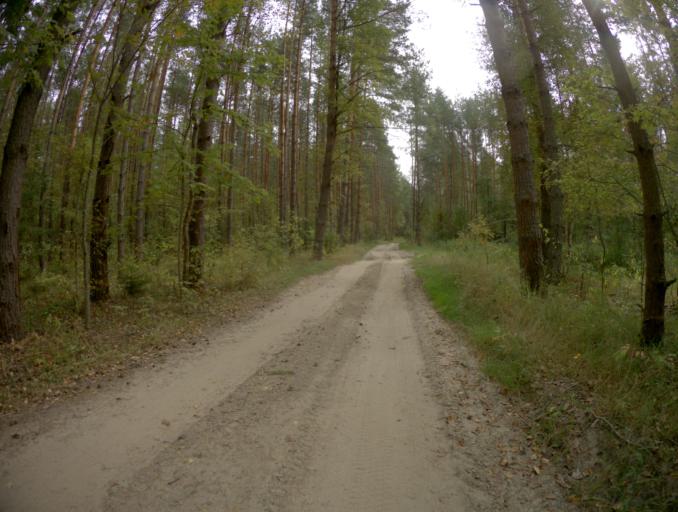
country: RU
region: Vladimir
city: Golovino
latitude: 55.9139
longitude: 40.4301
